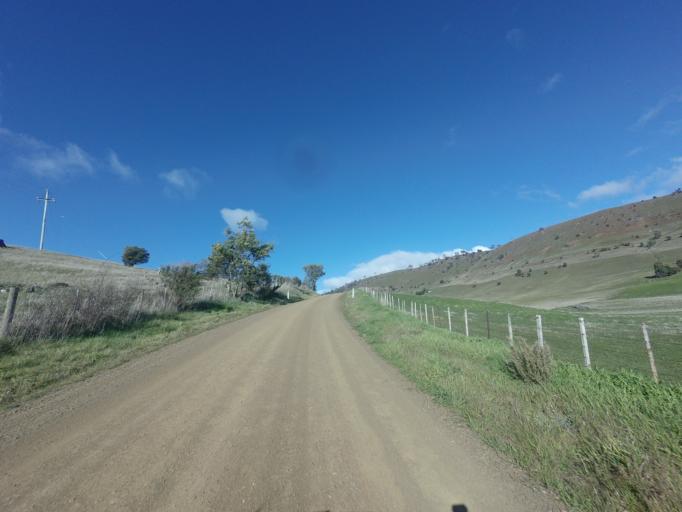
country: AU
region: Tasmania
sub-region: Derwent Valley
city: New Norfolk
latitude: -42.7023
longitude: 146.9899
